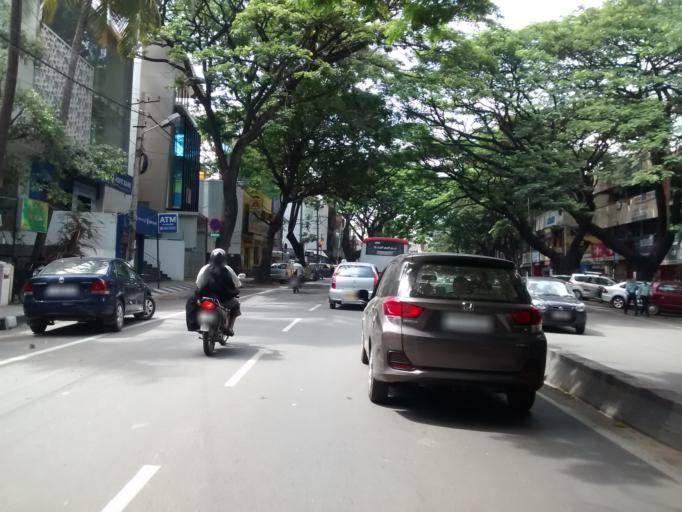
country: IN
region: Karnataka
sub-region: Bangalore Urban
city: Bangalore
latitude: 12.9994
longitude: 77.5526
